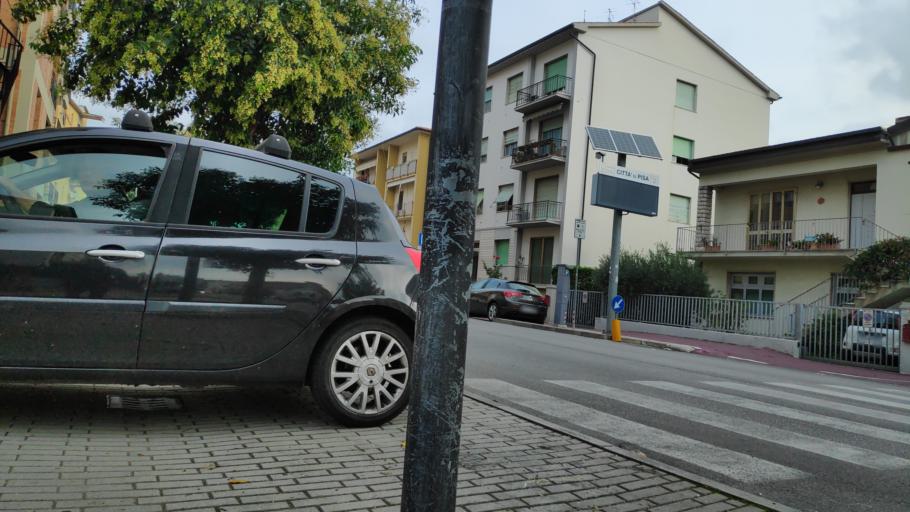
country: IT
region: Tuscany
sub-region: Province of Pisa
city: Pisa
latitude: 43.7033
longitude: 10.4009
